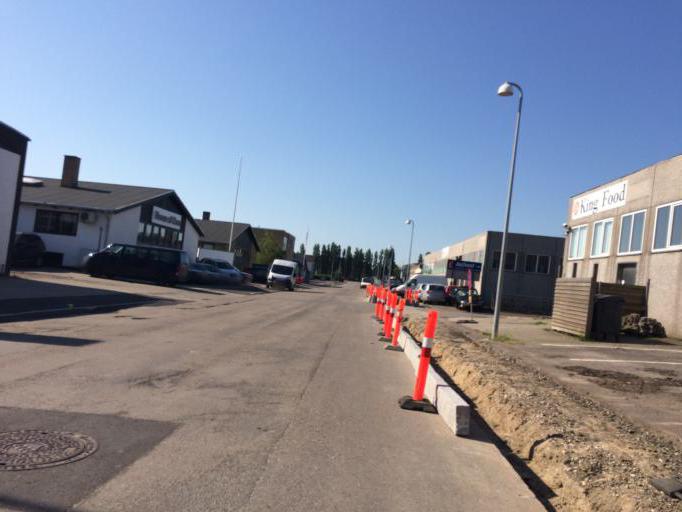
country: DK
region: Capital Region
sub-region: Hoje-Taastrup Kommune
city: Taastrup
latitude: 55.6491
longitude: 12.2879
